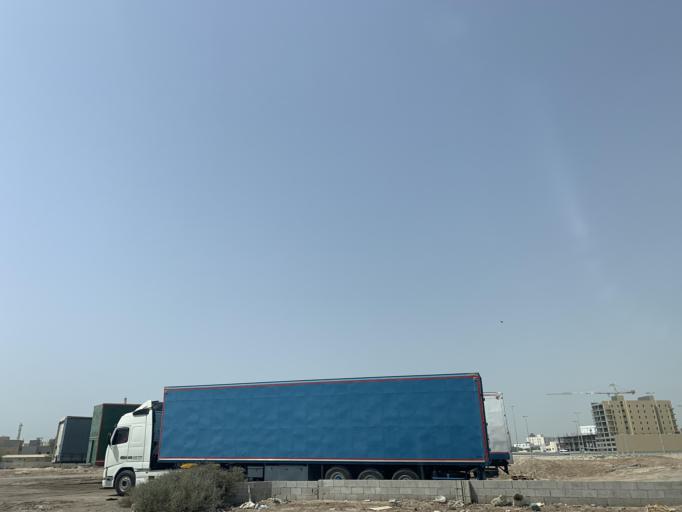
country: BH
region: Manama
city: Jidd Hafs
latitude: 26.2124
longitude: 50.5178
